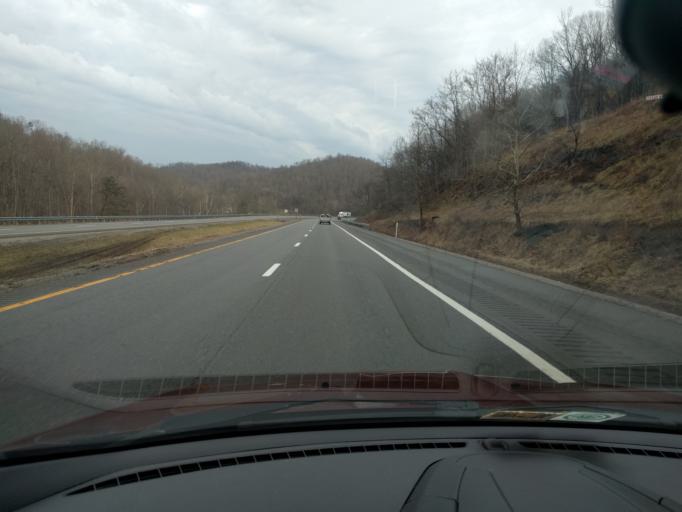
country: US
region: West Virginia
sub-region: Jackson County
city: Ravenswood
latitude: 38.9743
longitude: -81.6921
